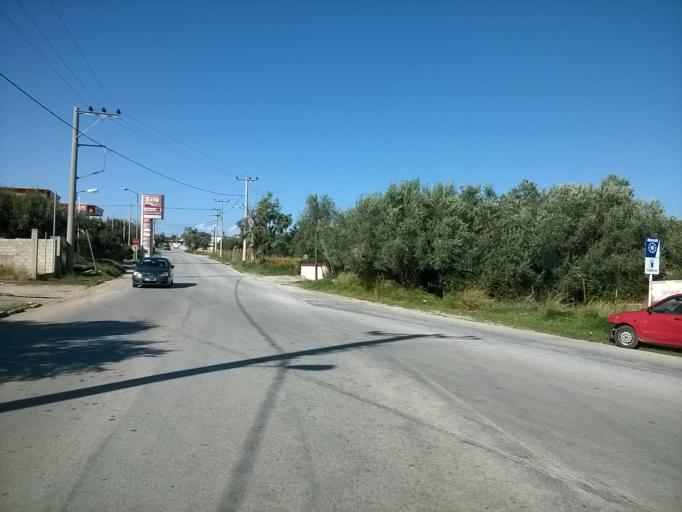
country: GR
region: Attica
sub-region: Nomarchia Anatolikis Attikis
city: Keratea
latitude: 37.8018
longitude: 23.9937
